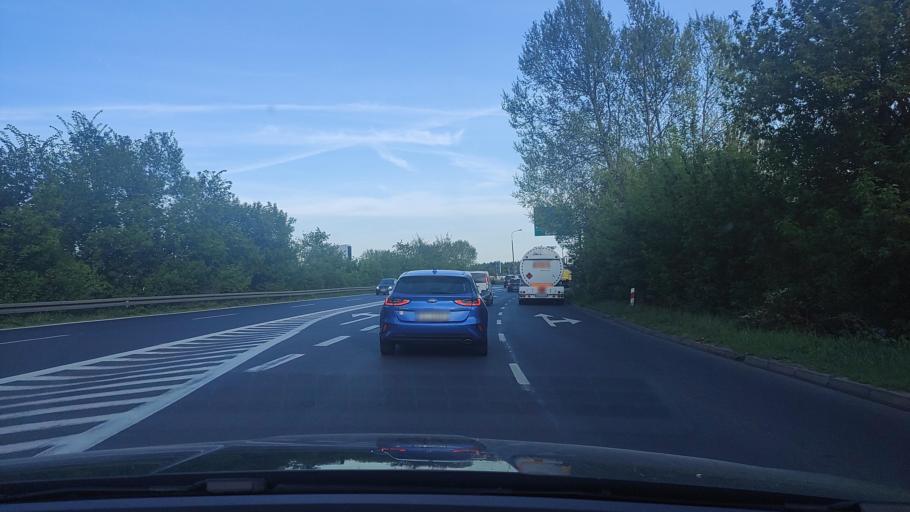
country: PL
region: Greater Poland Voivodeship
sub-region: Powiat poznanski
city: Czerwonak
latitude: 52.4314
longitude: 17.0078
